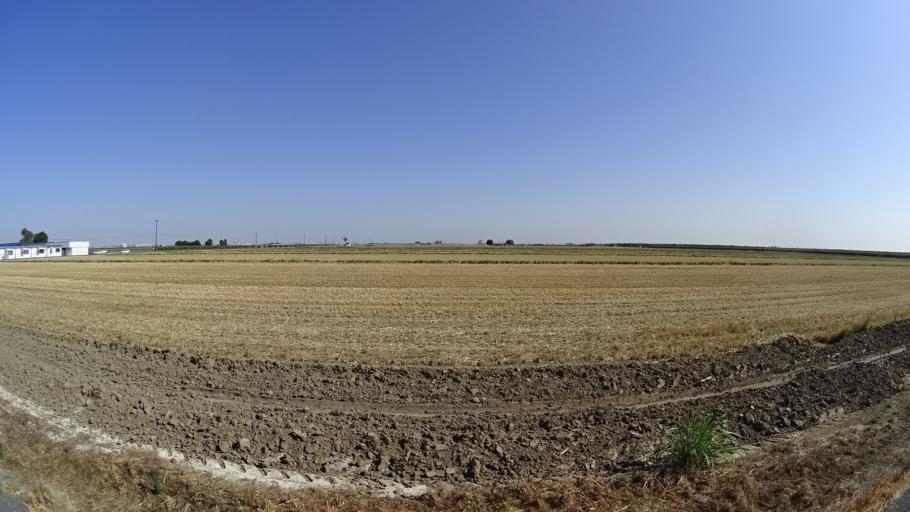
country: US
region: California
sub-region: Kings County
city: Home Garden
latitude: 36.2404
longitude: -119.6176
